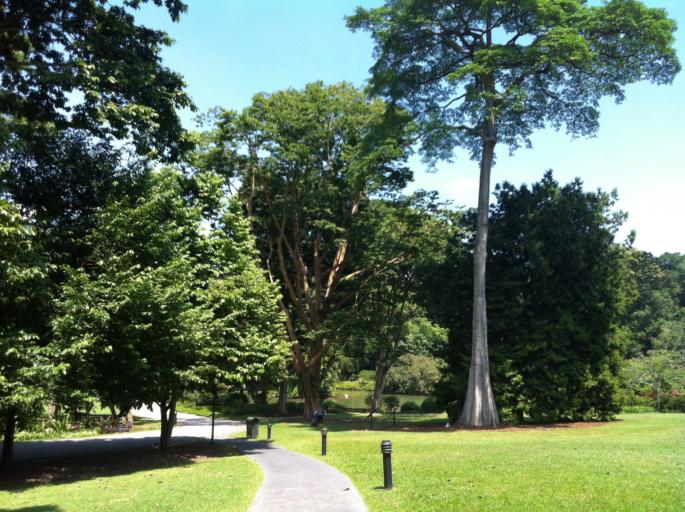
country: SG
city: Singapore
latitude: 1.3093
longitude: 103.8163
